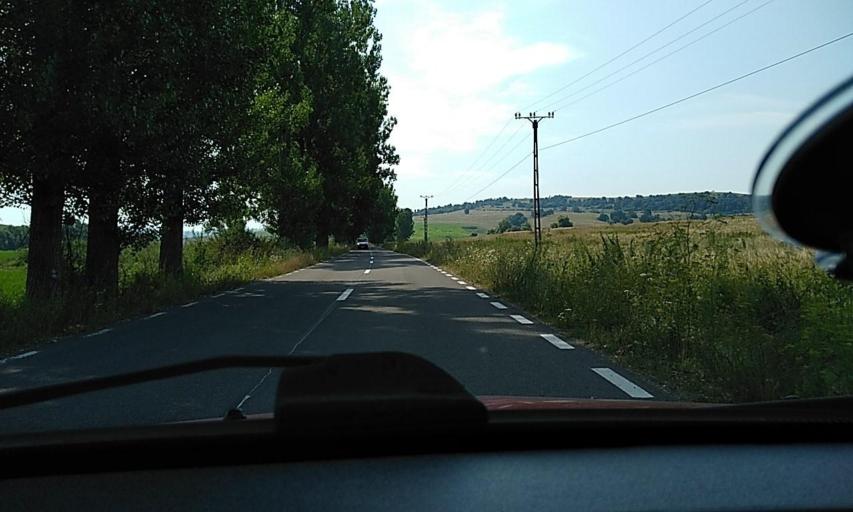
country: RO
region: Brasov
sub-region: Oras Rupea
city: Fiser
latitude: 46.0457
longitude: 25.1174
